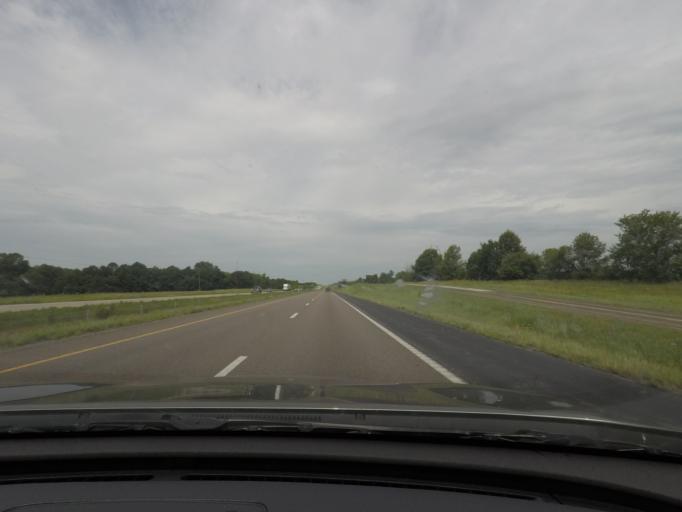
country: US
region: Missouri
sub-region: Callaway County
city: Fulton
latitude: 38.9251
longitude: -91.7731
